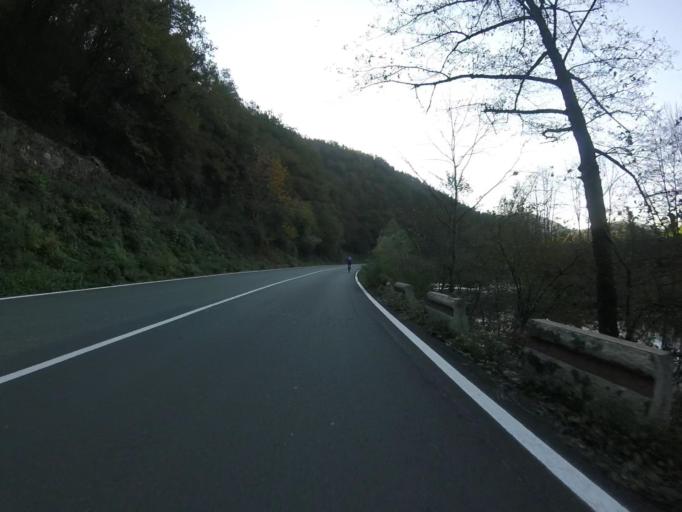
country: ES
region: Navarre
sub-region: Provincia de Navarra
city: Lesaka
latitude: 43.2471
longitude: -1.6695
